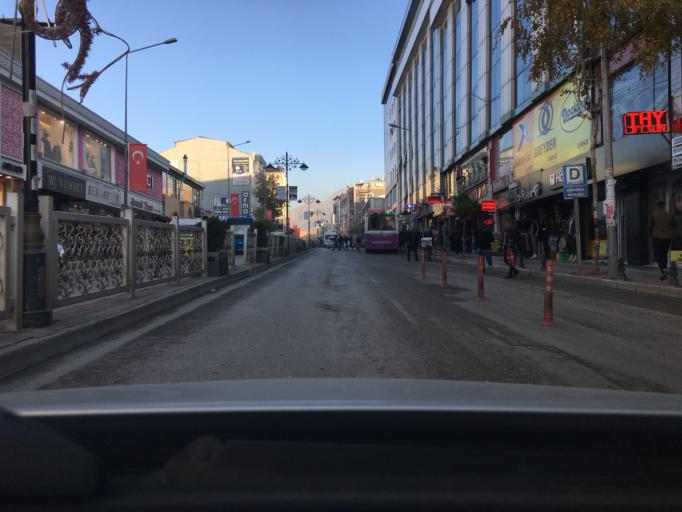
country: TR
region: Van
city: Van
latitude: 38.4986
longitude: 43.3945
